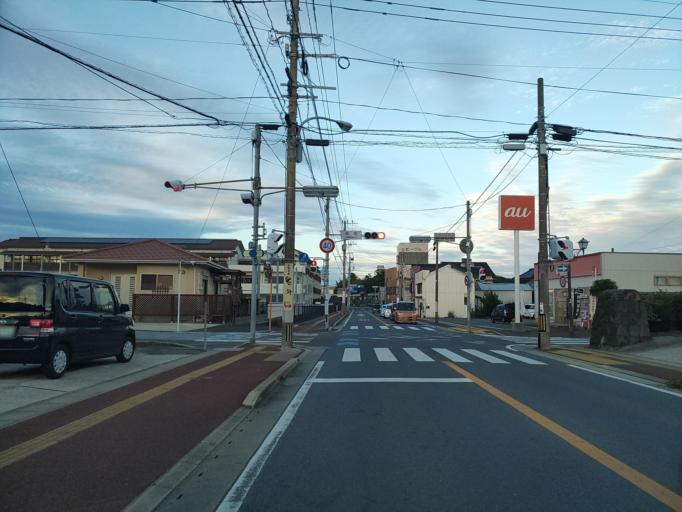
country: JP
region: Nagasaki
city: Fukuecho
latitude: 32.6916
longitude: 128.8424
